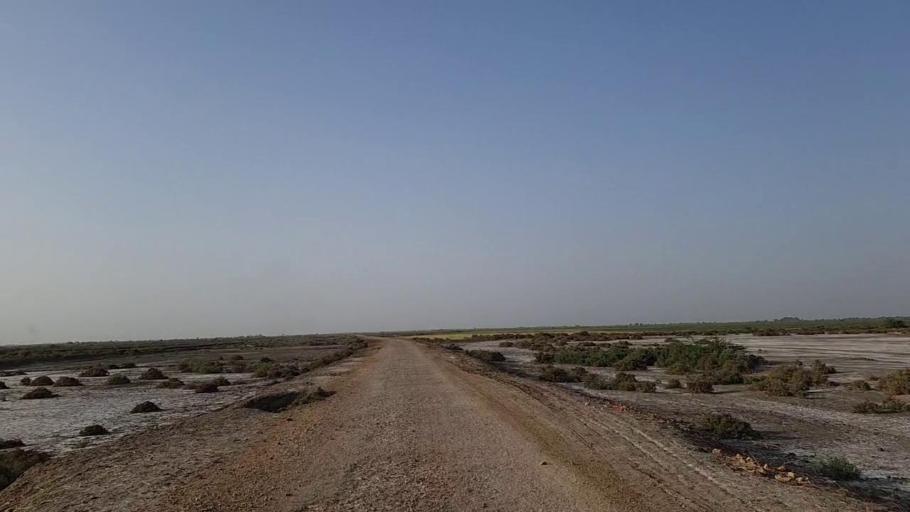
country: PK
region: Sindh
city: Jati
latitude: 24.3498
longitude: 68.1497
